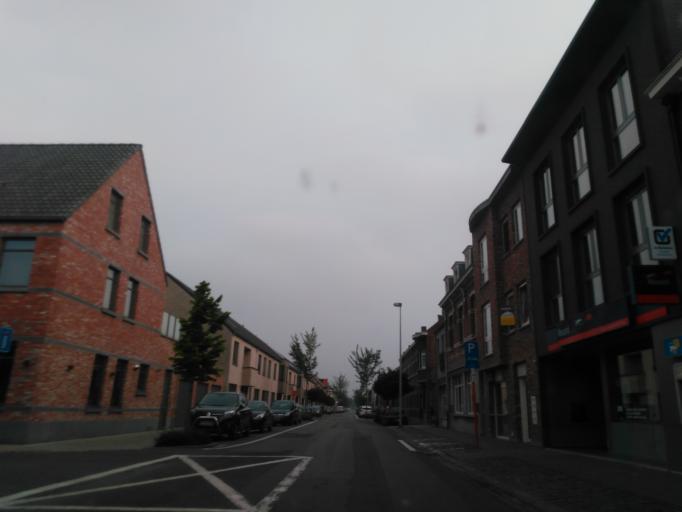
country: BE
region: Flanders
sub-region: Provincie Oost-Vlaanderen
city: Beveren
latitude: 51.2193
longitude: 4.2819
